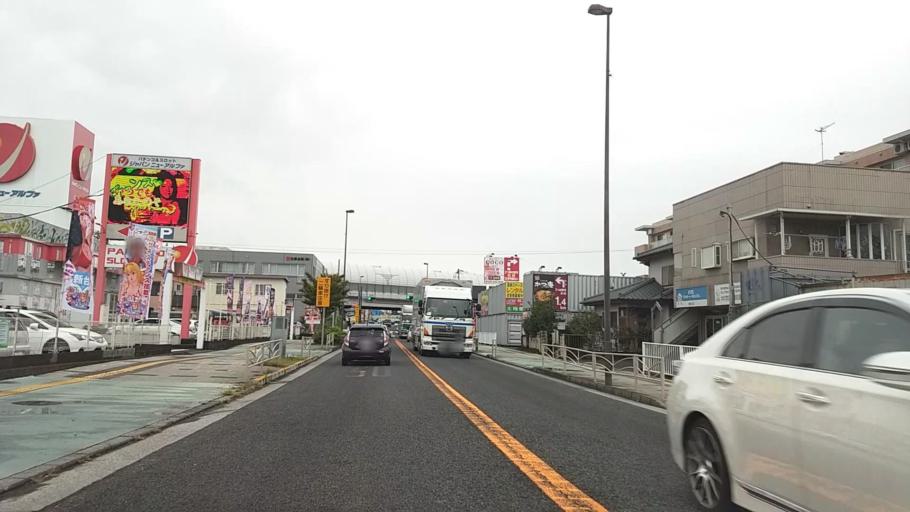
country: JP
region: Kanagawa
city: Atsugi
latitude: 35.4240
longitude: 139.3494
